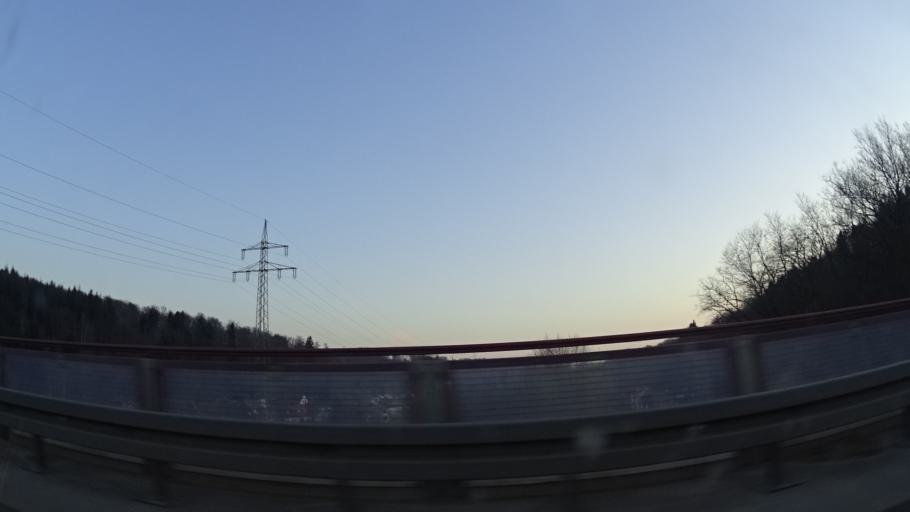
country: DE
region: Saarland
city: Sankt Ingbert
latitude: 49.2667
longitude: 7.0870
